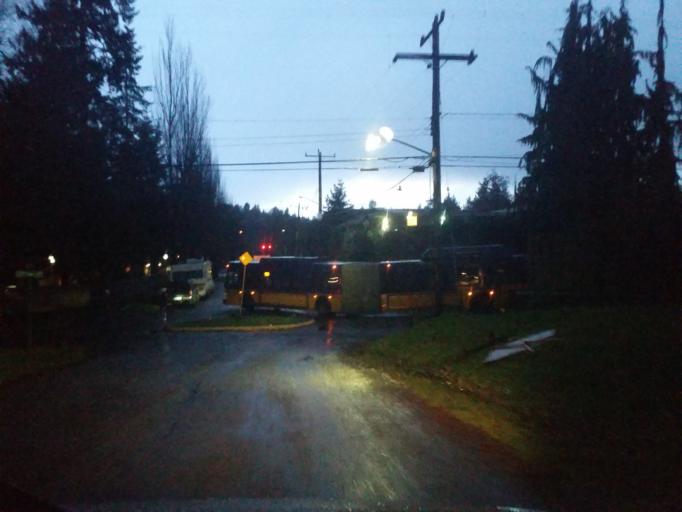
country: US
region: Washington
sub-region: King County
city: Lake Forest Park
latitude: 47.7321
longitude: -122.3095
